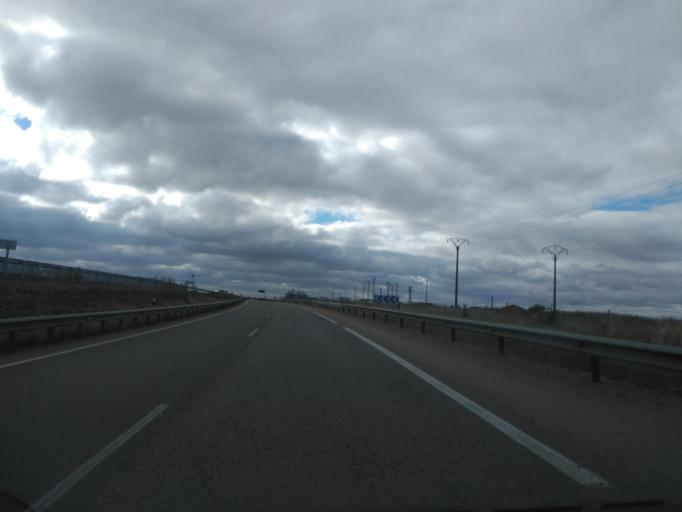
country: ES
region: Castille and Leon
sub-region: Provincia de Valladolid
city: Cubillas de Santa Marta
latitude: 41.7875
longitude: -4.6086
